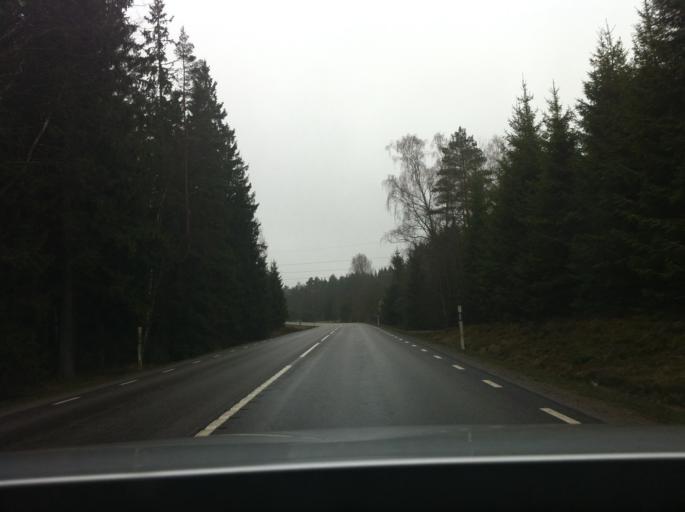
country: SE
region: Vaestra Goetaland
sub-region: Svenljunga Kommun
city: Svenljunga
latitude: 57.5269
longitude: 13.1121
